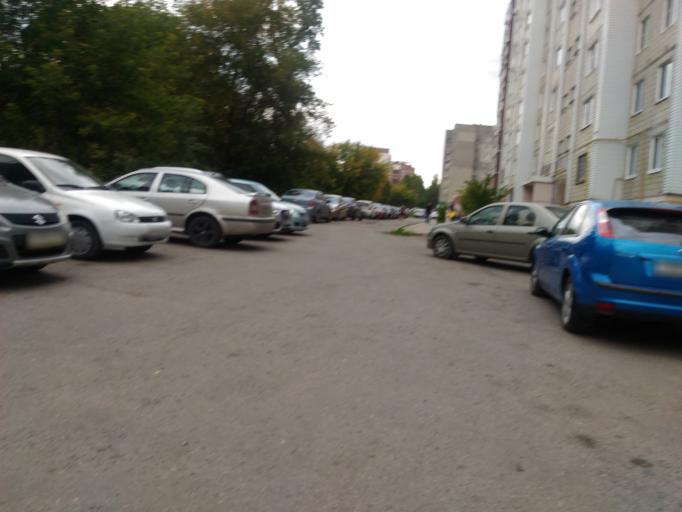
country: RU
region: Ulyanovsk
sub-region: Ulyanovskiy Rayon
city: Ulyanovsk
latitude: 54.2633
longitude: 48.3310
